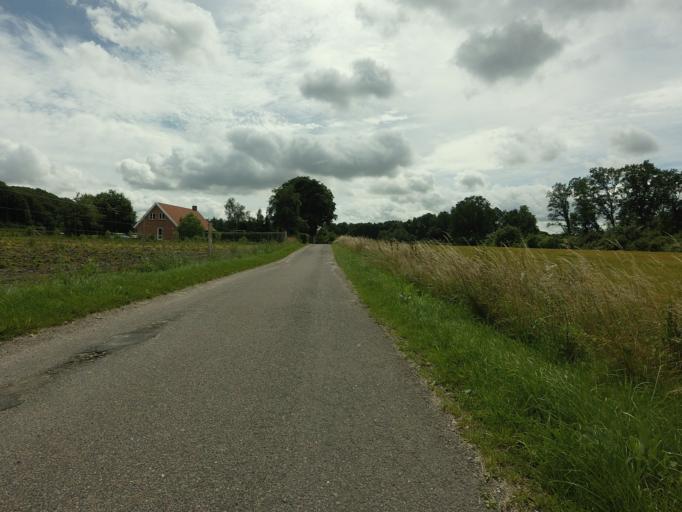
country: DK
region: Central Jutland
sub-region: Randers Kommune
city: Langa
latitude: 56.3659
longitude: 9.9037
